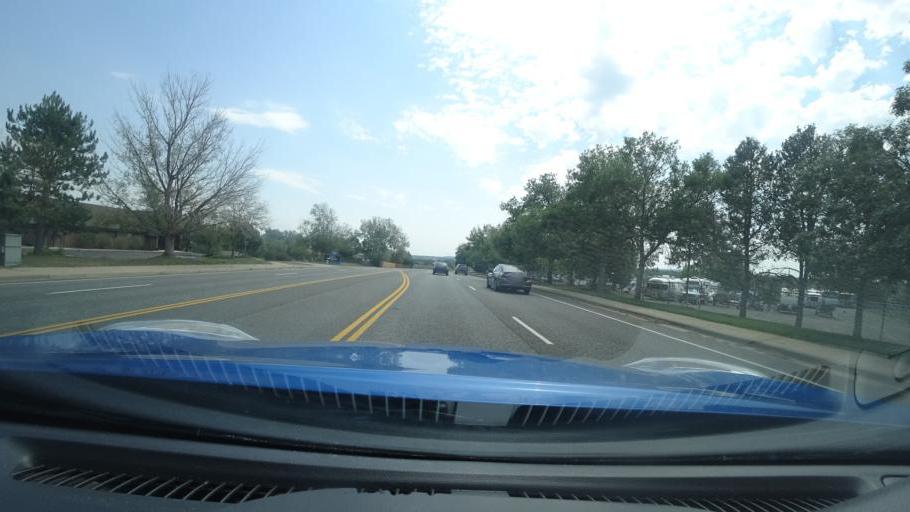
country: US
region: Colorado
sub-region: Adams County
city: Aurora
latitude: 39.6675
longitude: -104.8196
